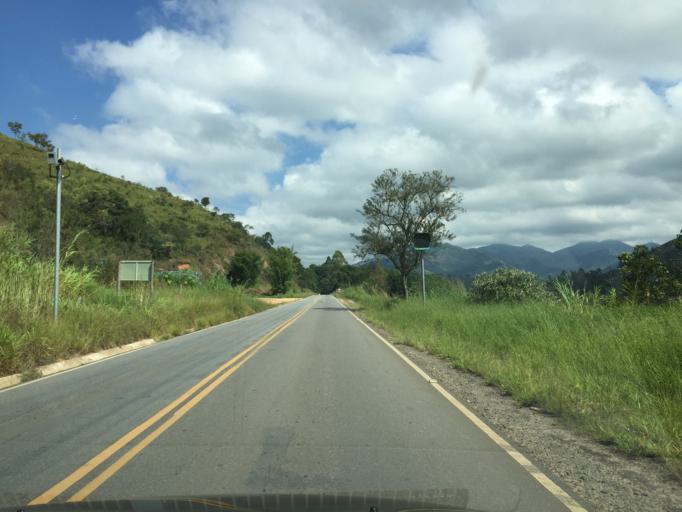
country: BR
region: Minas Gerais
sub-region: Passa Quatro
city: Passa Quatro
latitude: -22.3760
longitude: -44.9625
